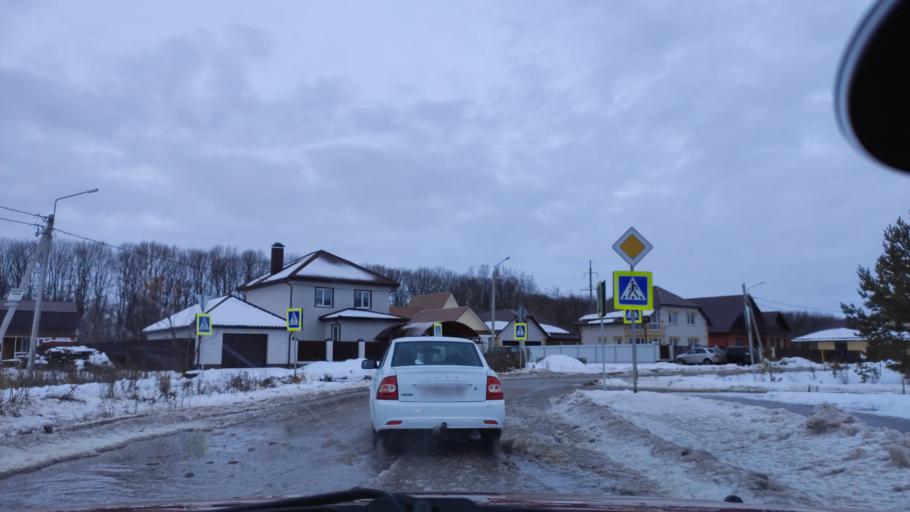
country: RU
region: Tambov
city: Tambov
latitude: 52.7590
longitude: 41.3716
